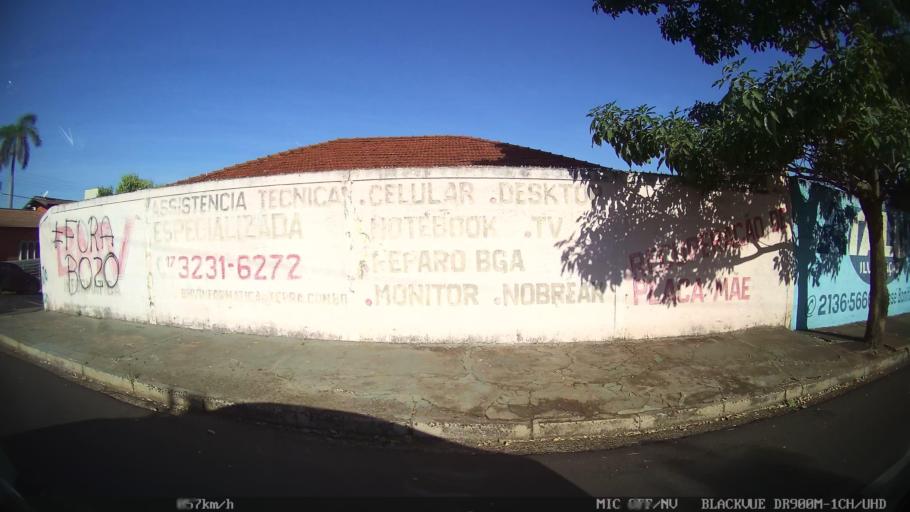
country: BR
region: Sao Paulo
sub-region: Sao Jose Do Rio Preto
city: Sao Jose do Rio Preto
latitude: -20.8134
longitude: -49.3989
